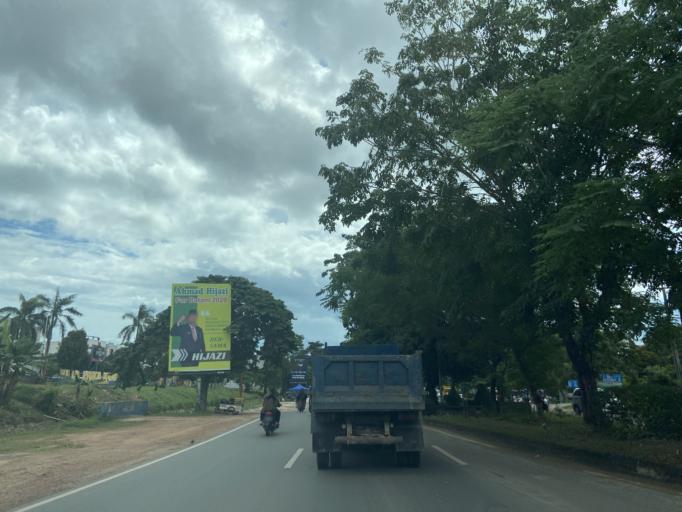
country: SG
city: Singapore
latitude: 1.0409
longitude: 103.9924
